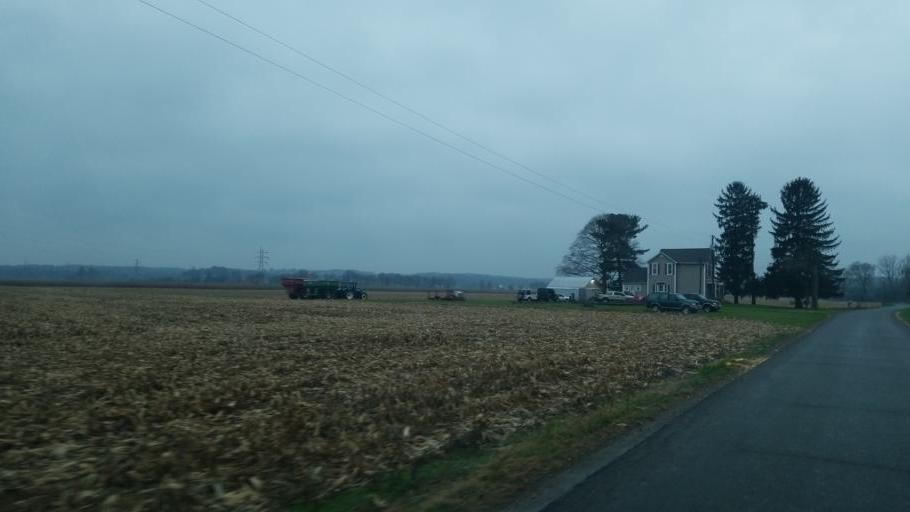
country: US
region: Ohio
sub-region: Knox County
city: Mount Vernon
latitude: 40.4092
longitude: -82.5183
